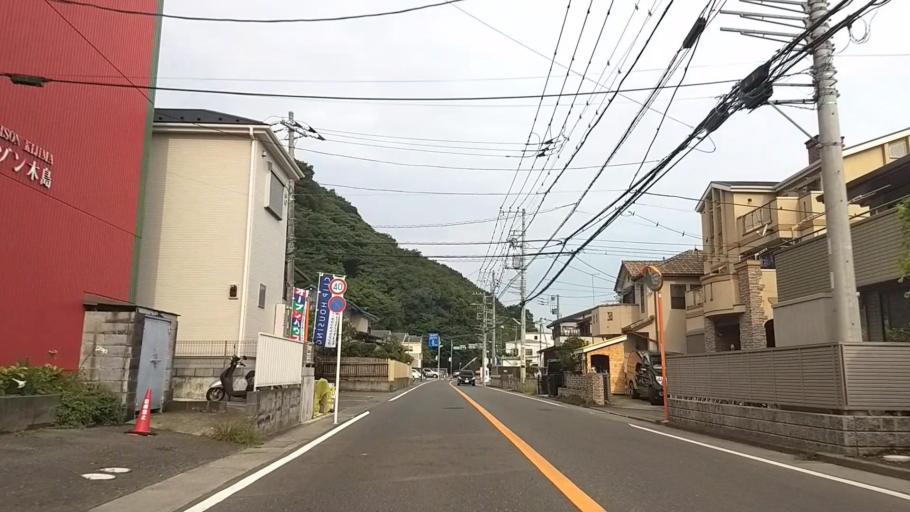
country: JP
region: Kanagawa
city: Hiratsuka
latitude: 35.3268
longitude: 139.3192
